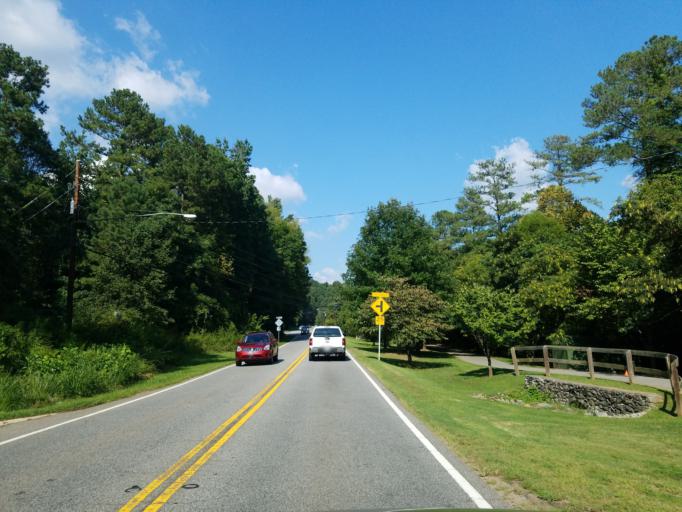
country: US
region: Georgia
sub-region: Fulton County
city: Roswell
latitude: 34.0094
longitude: -84.3409
